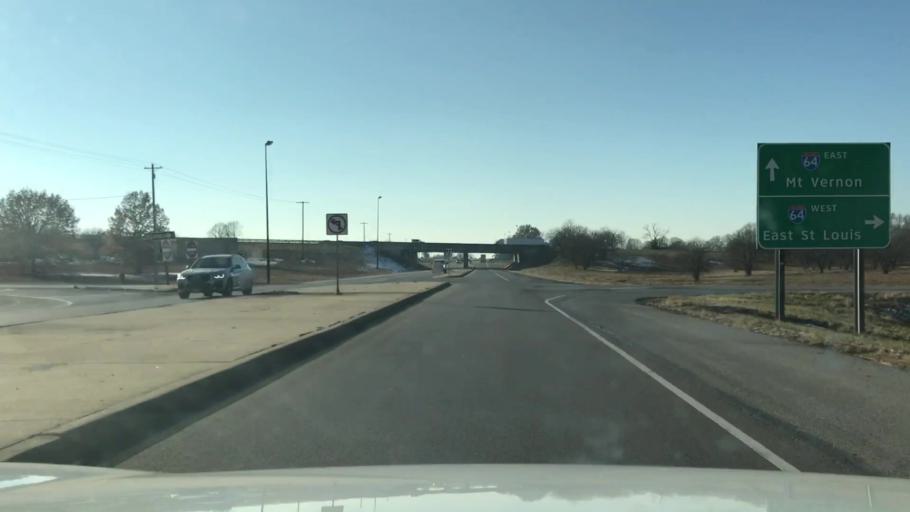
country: US
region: Illinois
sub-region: Clinton County
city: New Baden
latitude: 38.5355
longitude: -89.7256
